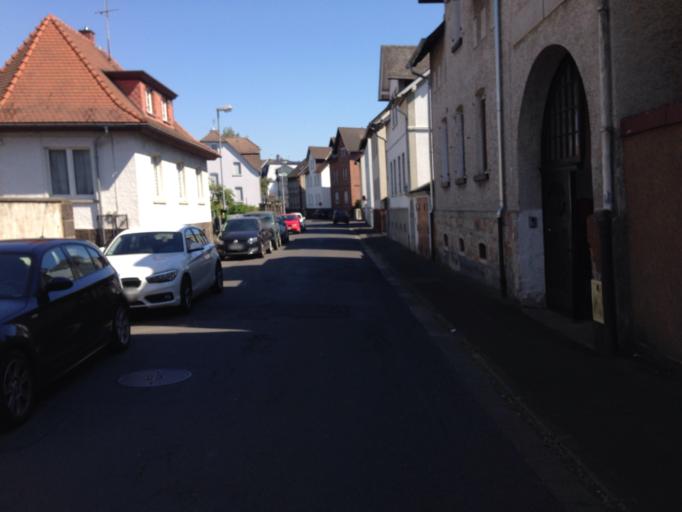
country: DE
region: Hesse
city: Lollar
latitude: 50.6500
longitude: 8.7066
